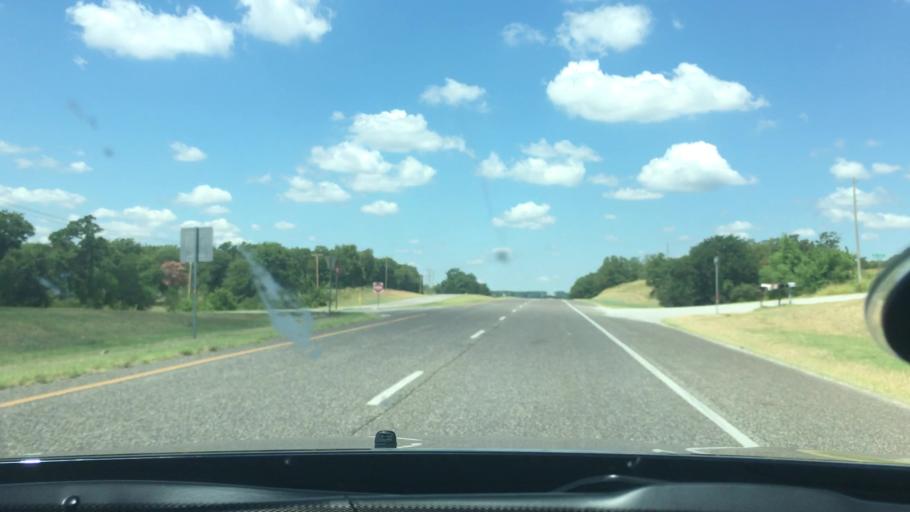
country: US
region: Oklahoma
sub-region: Carter County
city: Lone Grove
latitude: 34.1730
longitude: -97.3434
